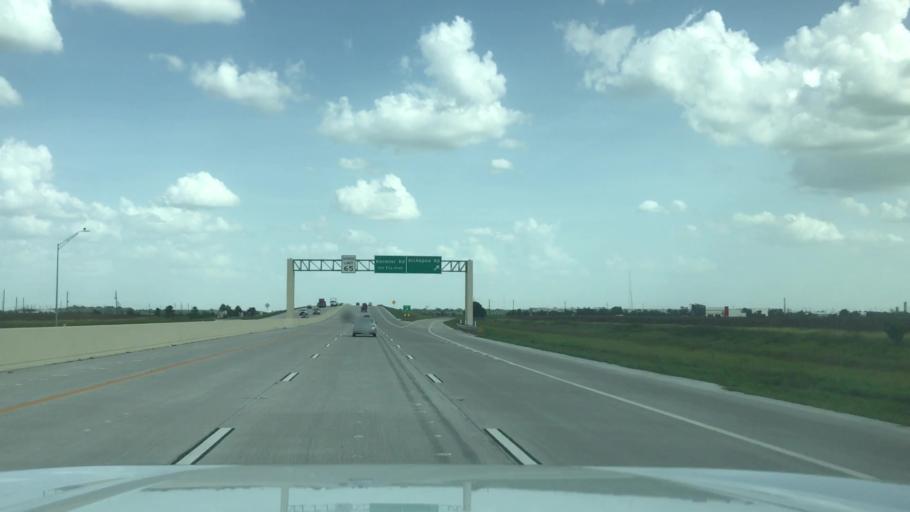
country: US
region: Texas
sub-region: Waller County
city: Waller
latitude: 30.0510
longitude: -95.8794
